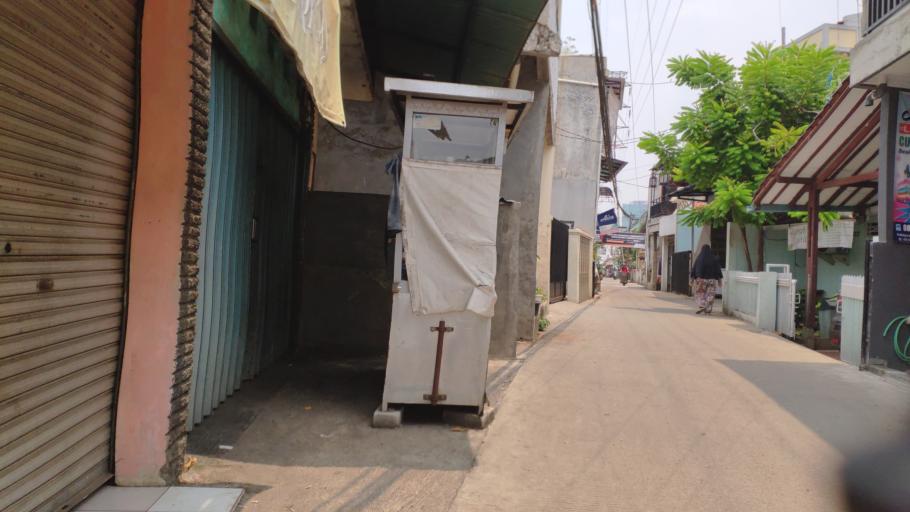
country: ID
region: West Java
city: Depok
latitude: -6.3089
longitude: 106.8312
